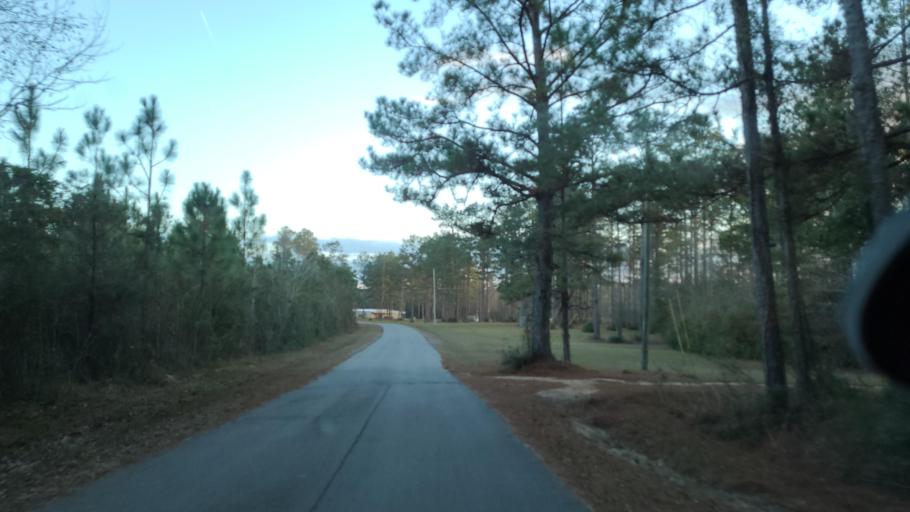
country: US
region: Mississippi
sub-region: Perry County
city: New Augusta
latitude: 31.1318
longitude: -89.2047
